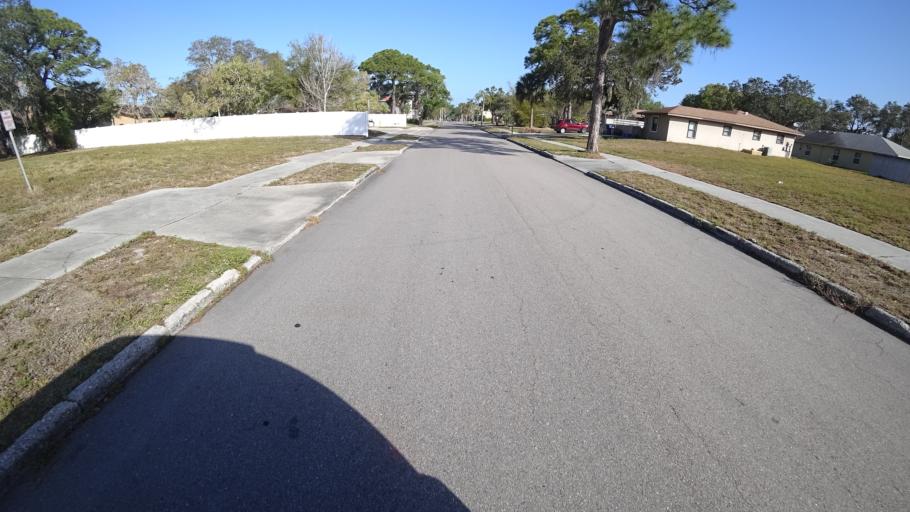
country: US
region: Florida
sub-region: Manatee County
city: Whitfield
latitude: 27.4086
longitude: -82.5689
